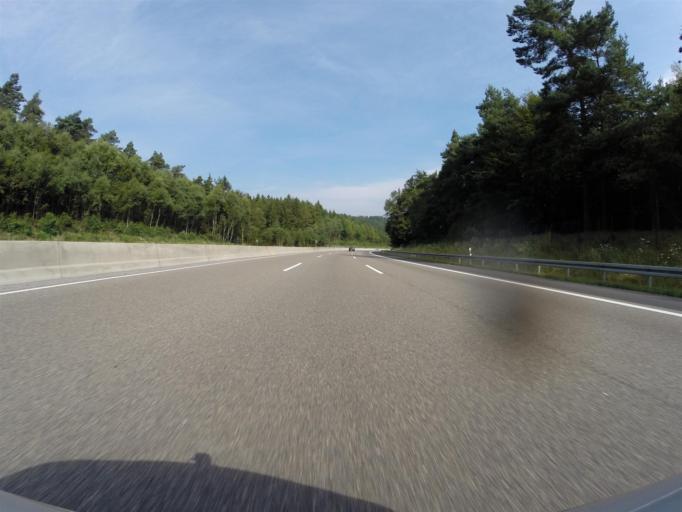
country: DE
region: Hesse
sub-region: Regierungsbezirk Kassel
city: Kirchheim
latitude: 50.9035
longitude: 9.5856
